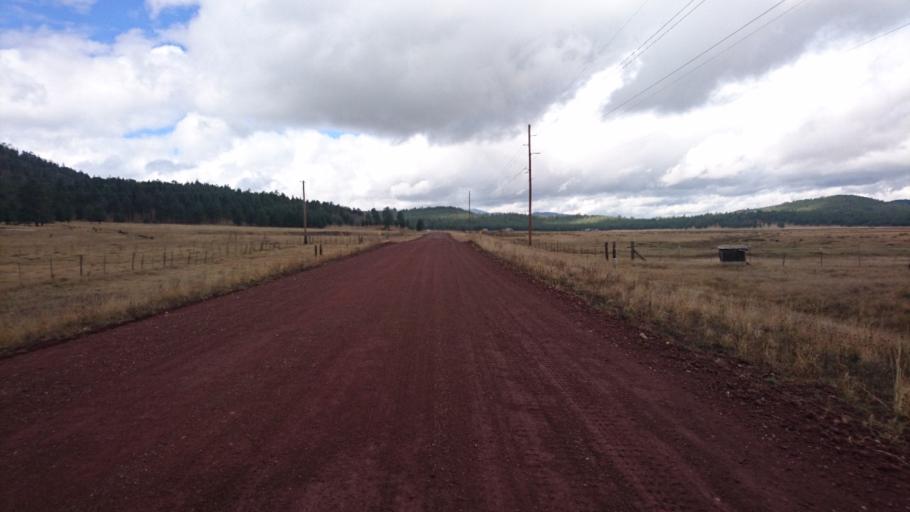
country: US
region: Arizona
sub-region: Coconino County
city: Parks
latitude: 35.2667
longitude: -111.8810
